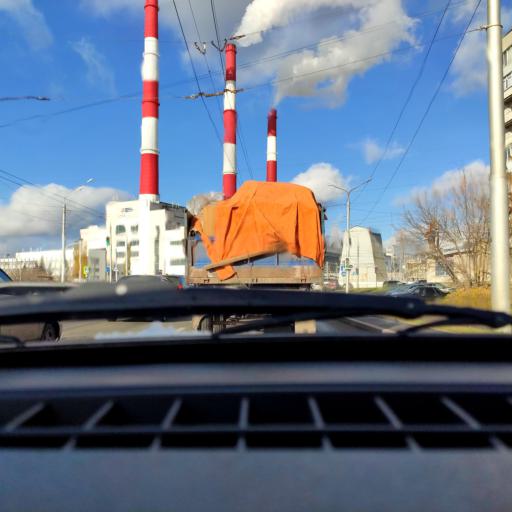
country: RU
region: Bashkortostan
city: Ufa
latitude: 54.7870
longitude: 56.1224
